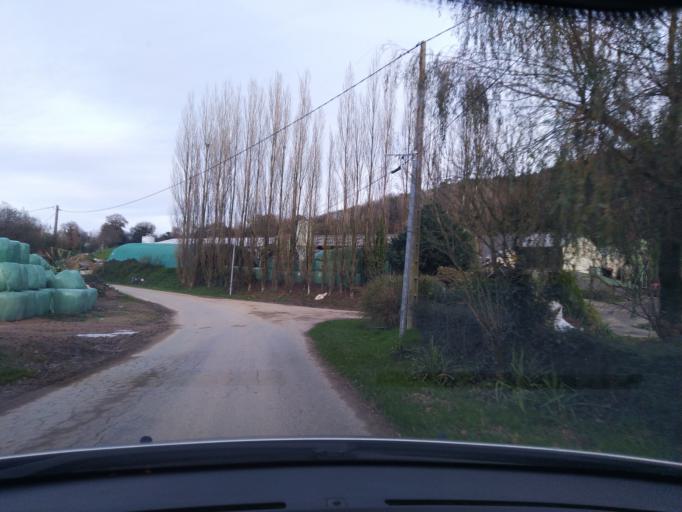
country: FR
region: Brittany
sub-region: Departement du Finistere
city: Guerlesquin
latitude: 48.5551
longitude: -3.6191
